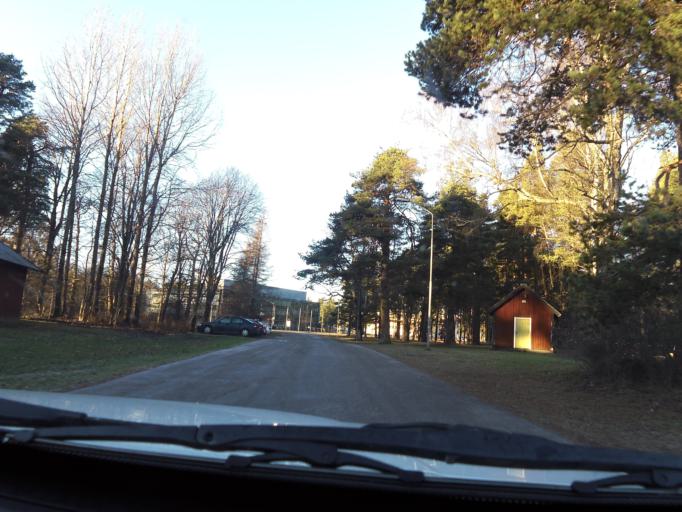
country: SE
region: Gaevleborg
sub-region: Gavle Kommun
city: Gavle
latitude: 60.6691
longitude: 17.1119
